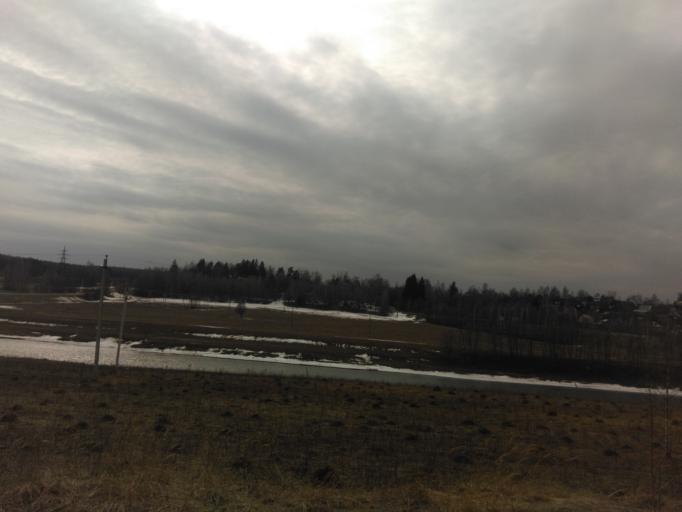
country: RU
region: Moskovskaya
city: Tuchkovo
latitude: 55.6144
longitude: 36.4216
